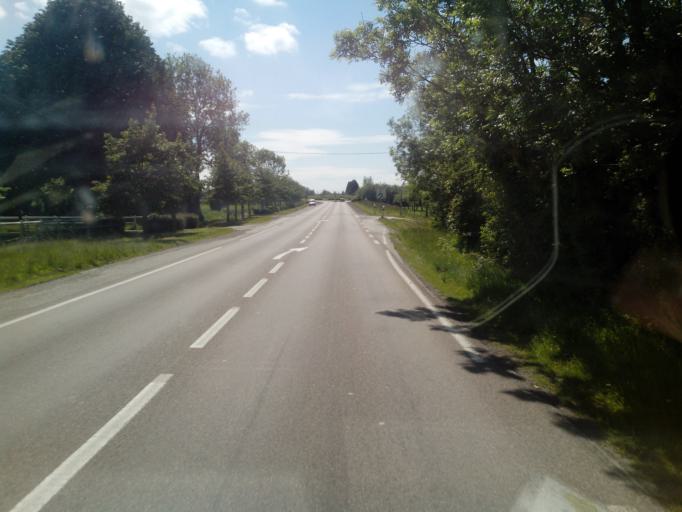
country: FR
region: Haute-Normandie
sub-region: Departement de l'Eure
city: Beuzeville
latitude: 49.3517
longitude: 0.3742
